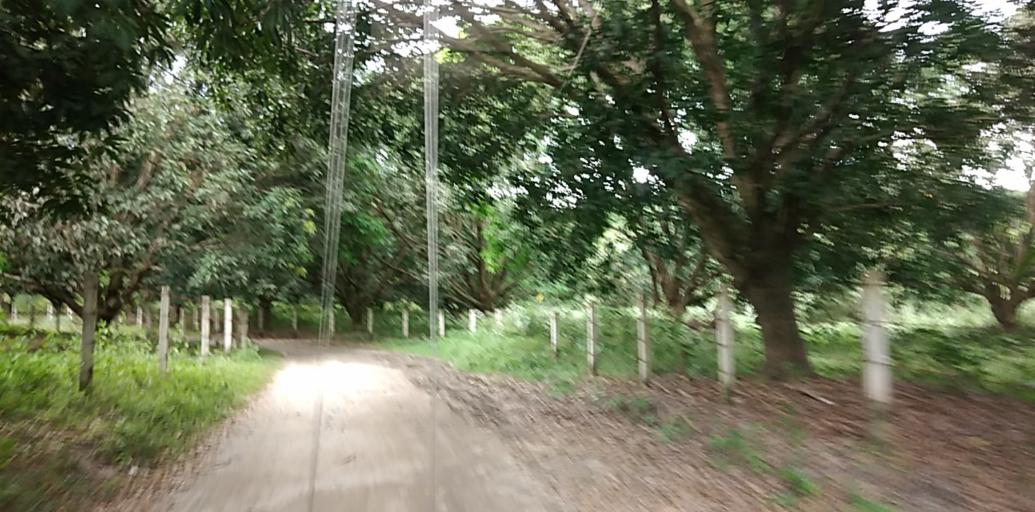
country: PH
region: Central Luzon
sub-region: Province of Pampanga
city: Babo-Pangulo
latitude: 15.1106
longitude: 120.4932
